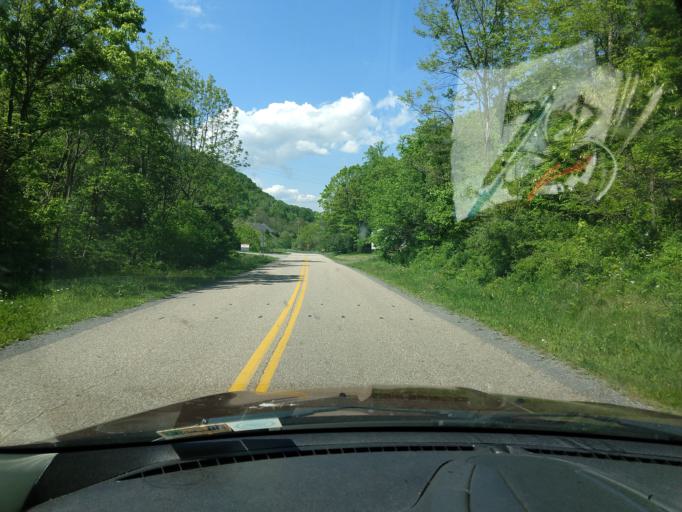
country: US
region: Virginia
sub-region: City of Covington
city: Fairlawn
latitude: 37.7325
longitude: -79.9139
